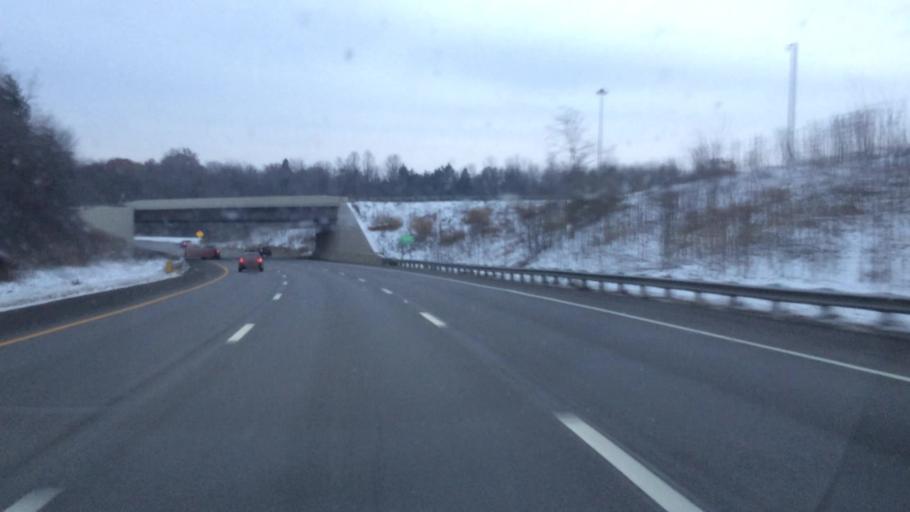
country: US
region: Ohio
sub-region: Summit County
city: Montrose-Ghent
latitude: 41.1214
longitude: -81.6516
